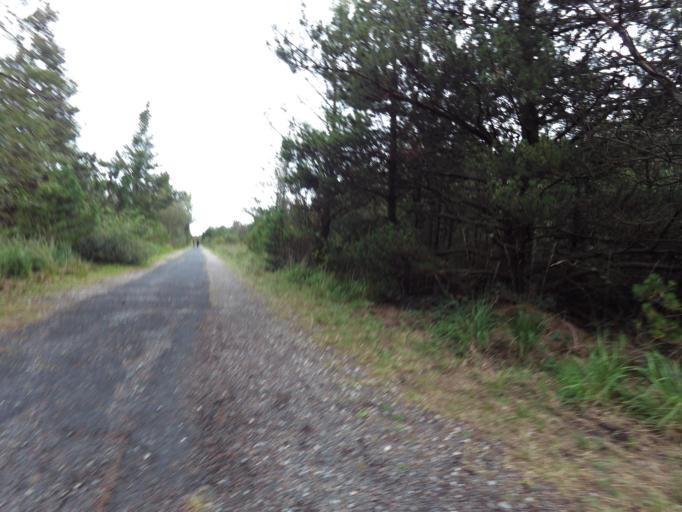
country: IE
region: Leinster
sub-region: Uibh Fhaili
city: Ferbane
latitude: 53.2174
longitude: -7.7519
